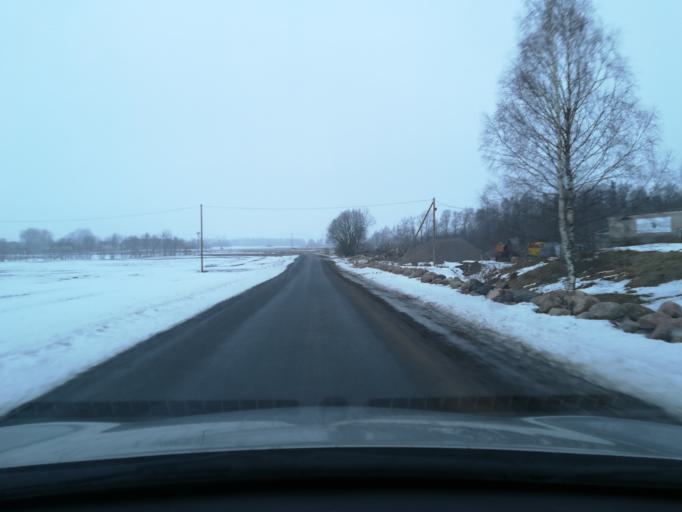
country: EE
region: Harju
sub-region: Raasiku vald
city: Raasiku
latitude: 59.3532
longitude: 25.2064
